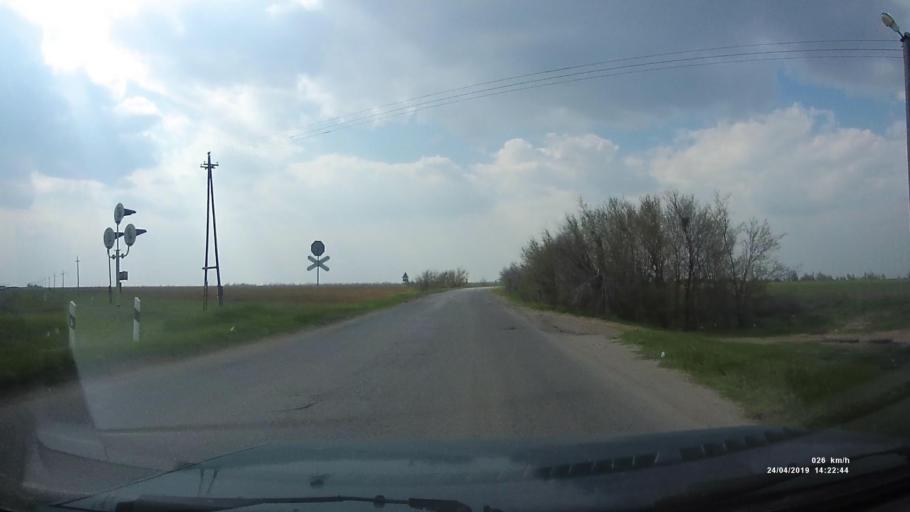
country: RU
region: Kalmykiya
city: Arshan'
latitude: 46.3176
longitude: 44.1221
